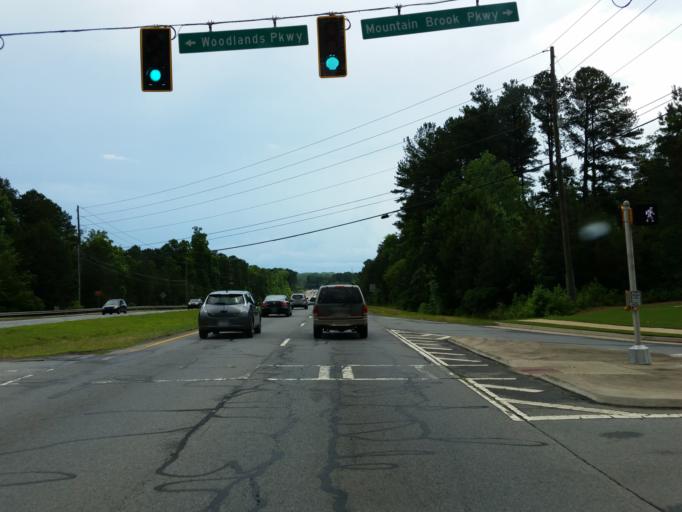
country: US
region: Georgia
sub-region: Cherokee County
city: Woodstock
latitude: 34.0849
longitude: -84.4617
